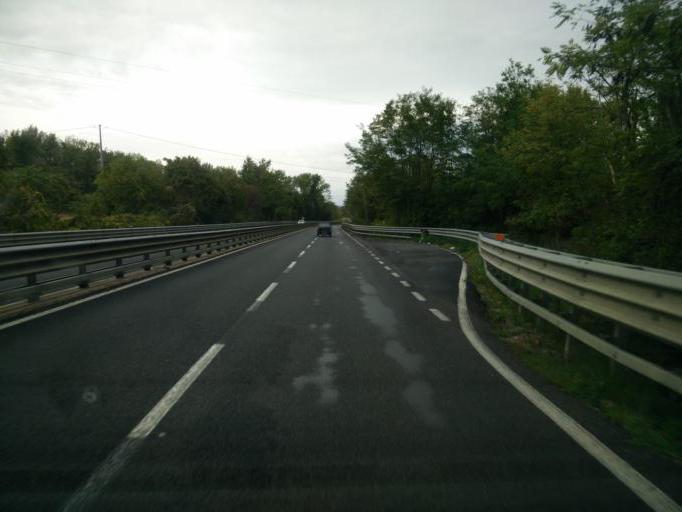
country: IT
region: Tuscany
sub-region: Province of Florence
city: Sambuca
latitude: 43.6026
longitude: 11.1924
